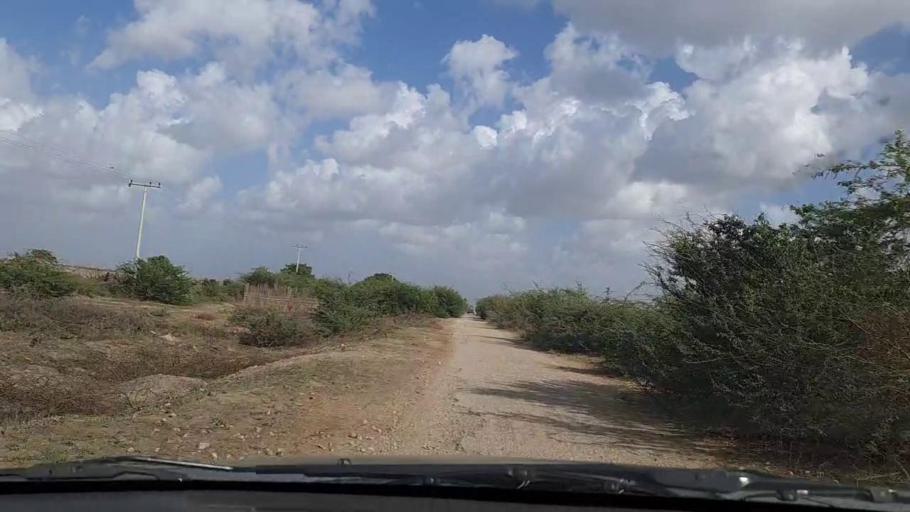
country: PK
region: Sindh
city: Keti Bandar
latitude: 24.0976
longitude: 67.6045
